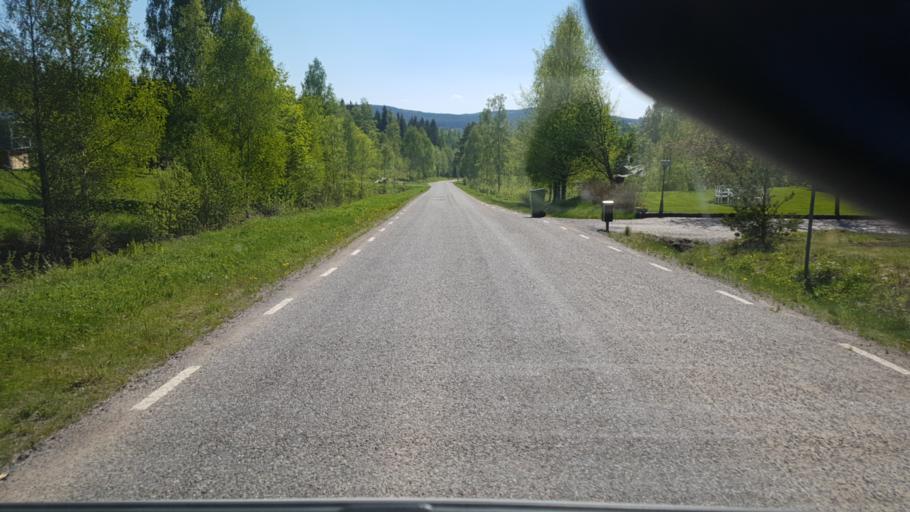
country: SE
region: Vaermland
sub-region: Eda Kommun
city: Charlottenberg
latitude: 59.9777
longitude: 12.4119
